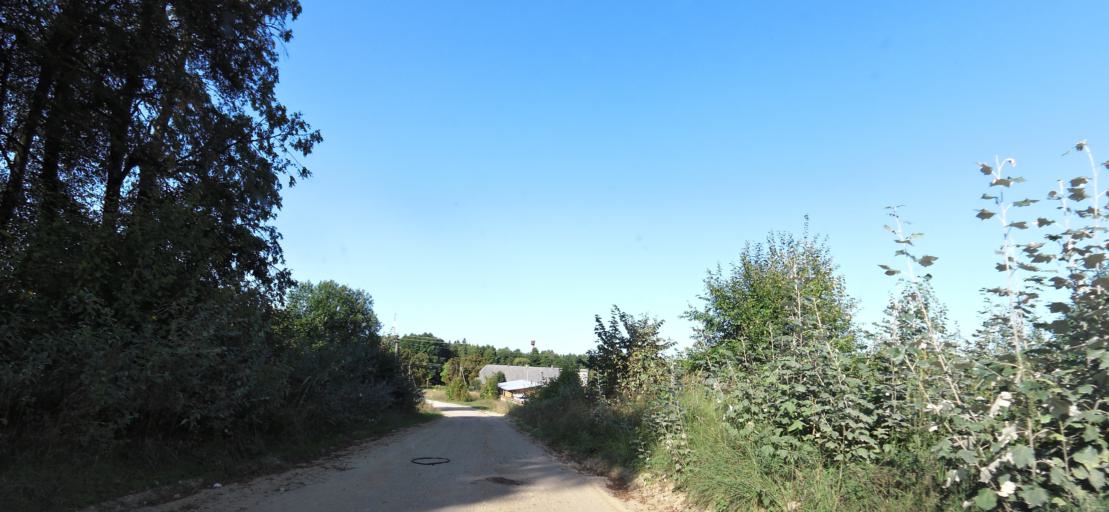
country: LT
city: Salcininkai
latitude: 54.4318
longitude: 25.3006
